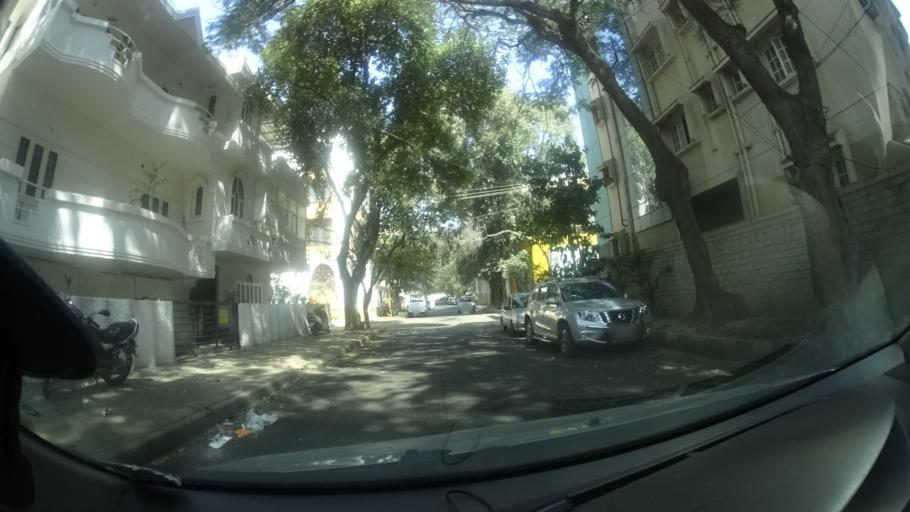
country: IN
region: Karnataka
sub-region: Bangalore Urban
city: Bangalore
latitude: 13.0132
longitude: 77.5785
